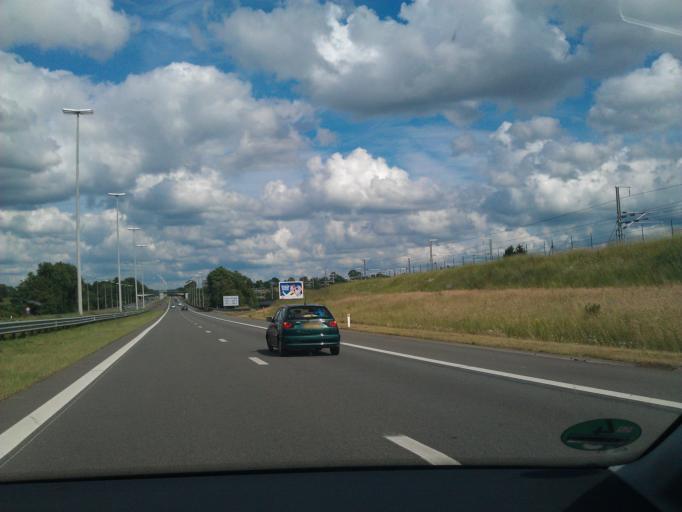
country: BE
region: Wallonia
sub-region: Province de Liege
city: Welkenraedt
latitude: 50.6488
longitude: 5.9524
